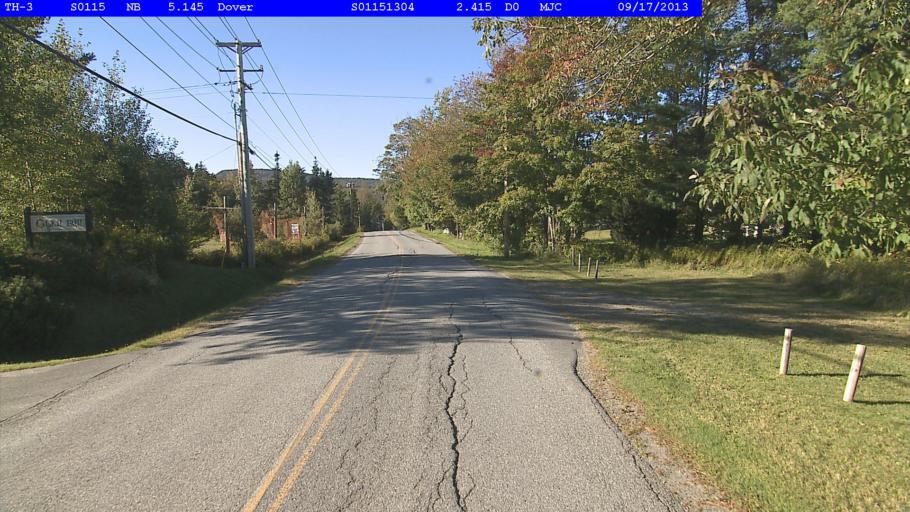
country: US
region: Vermont
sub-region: Windham County
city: Dover
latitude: 42.9592
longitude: -72.8884
